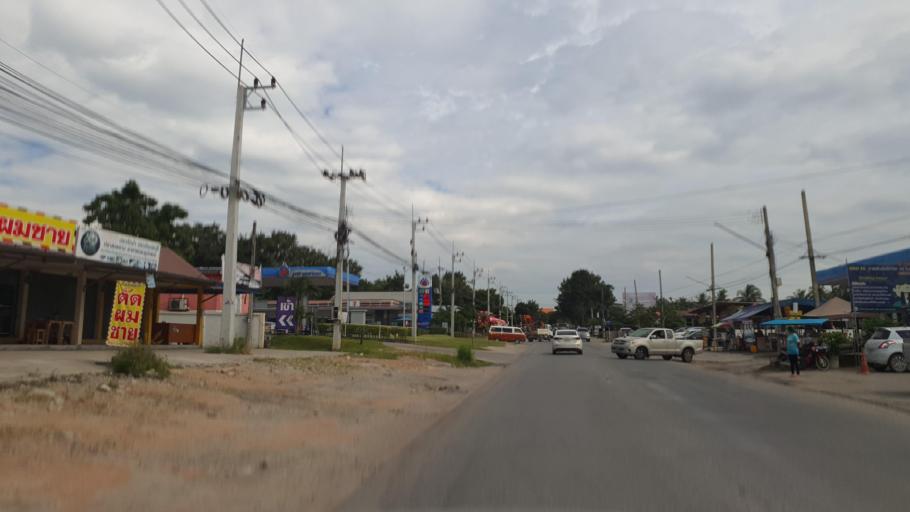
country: TH
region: Chon Buri
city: Phatthaya
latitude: 12.9430
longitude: 100.9452
